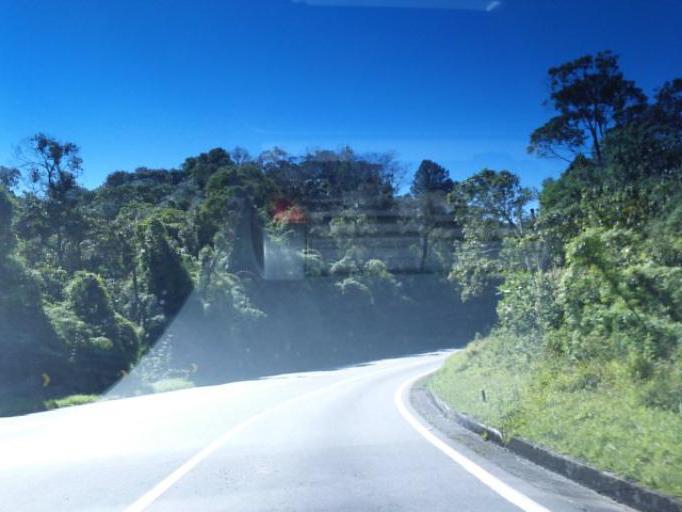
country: BR
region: Sao Paulo
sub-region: Campos Do Jordao
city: Campos do Jordao
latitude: -22.8228
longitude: -45.6256
